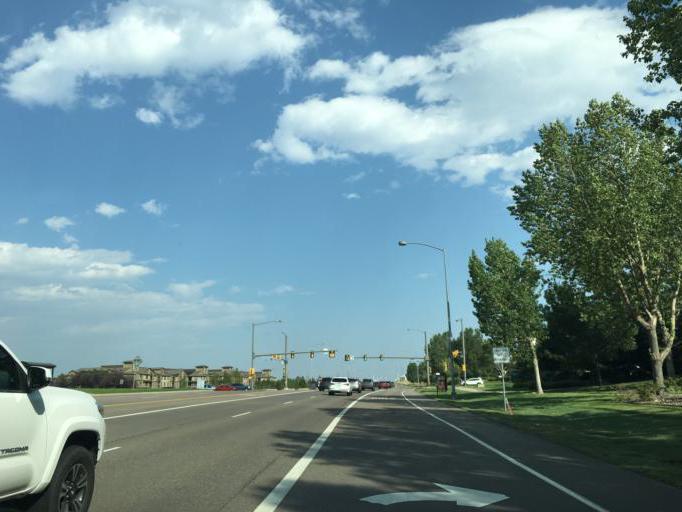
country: US
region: Colorado
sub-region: Broomfield County
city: Broomfield
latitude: 39.9163
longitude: -105.1072
